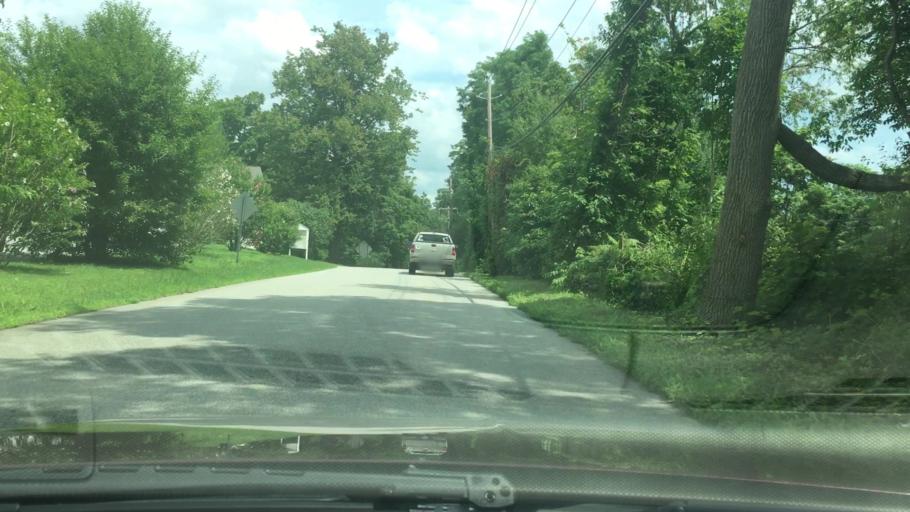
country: US
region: New York
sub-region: Dutchess County
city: Pawling
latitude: 41.6116
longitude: -73.6796
